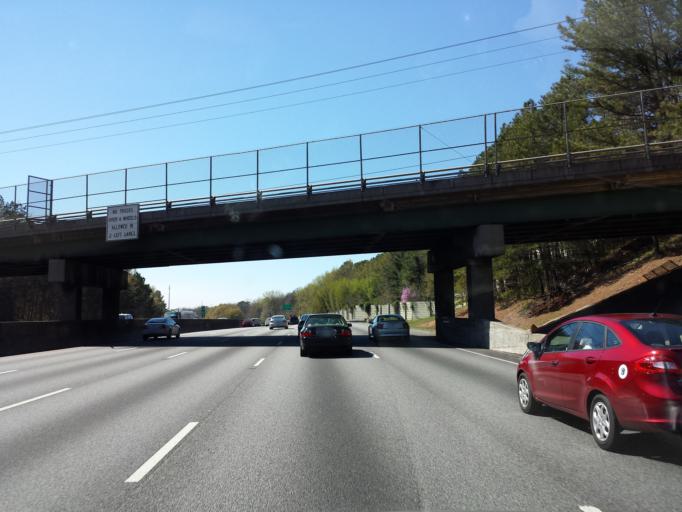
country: US
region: Georgia
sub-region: Fulton County
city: Sandy Springs
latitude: 33.9149
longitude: -84.4001
